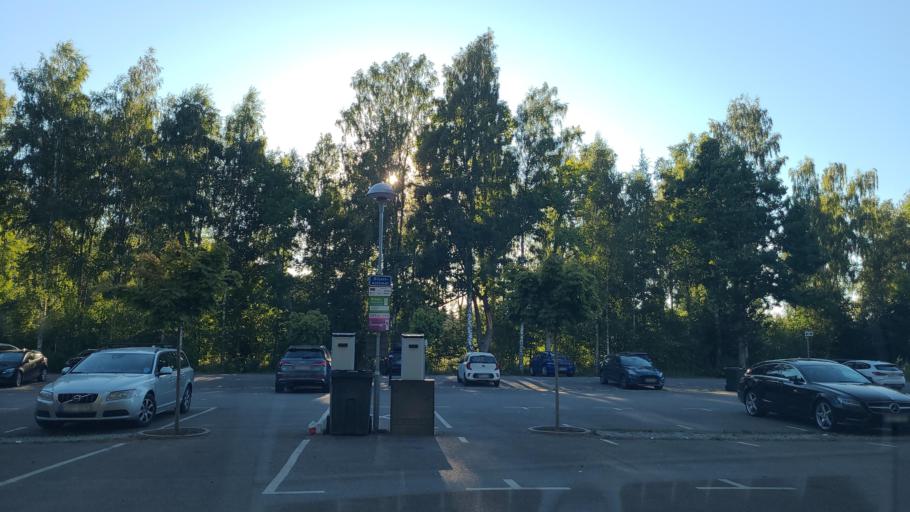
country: SE
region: Kalmar
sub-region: Borgholms Kommun
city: Borgholm
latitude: 57.2752
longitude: 17.0478
